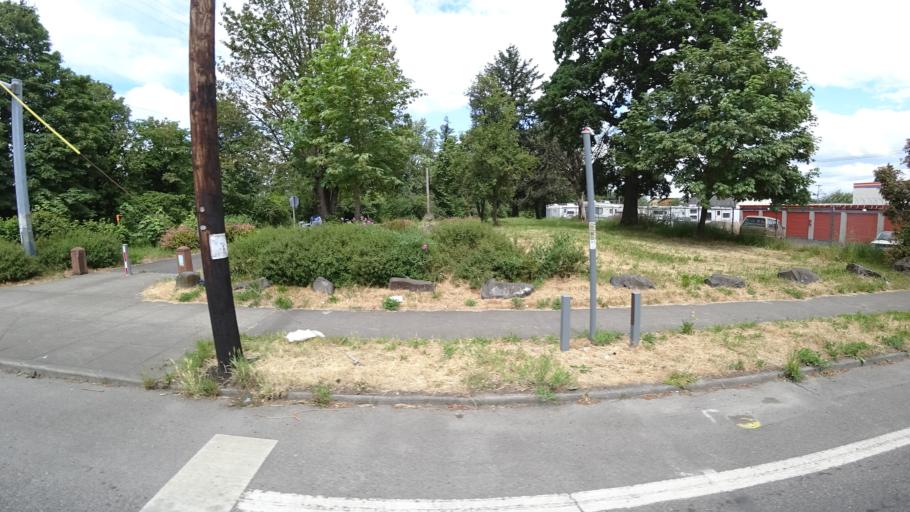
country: US
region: Oregon
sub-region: Washington County
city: West Haven
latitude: 45.5861
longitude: -122.7347
